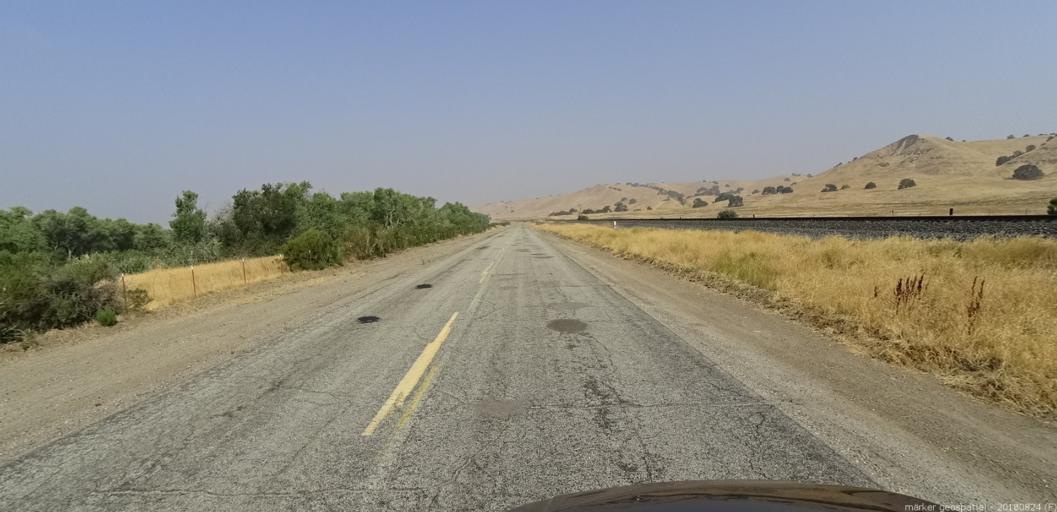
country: US
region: California
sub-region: San Luis Obispo County
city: San Miguel
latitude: 35.8548
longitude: -120.7603
